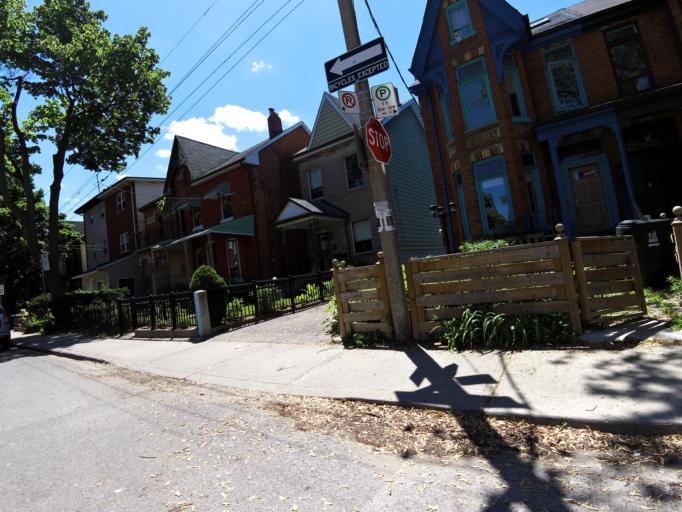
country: CA
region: Ontario
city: Toronto
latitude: 43.6537
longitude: -79.4031
